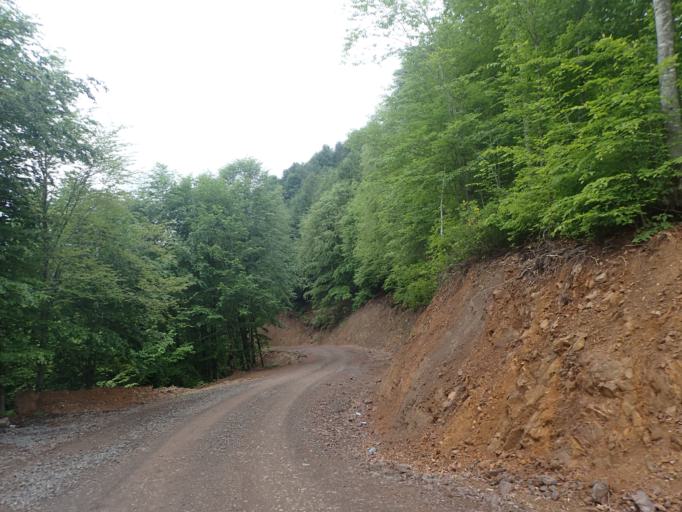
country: TR
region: Samsun
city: Salipazari
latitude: 40.9137
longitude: 36.8699
